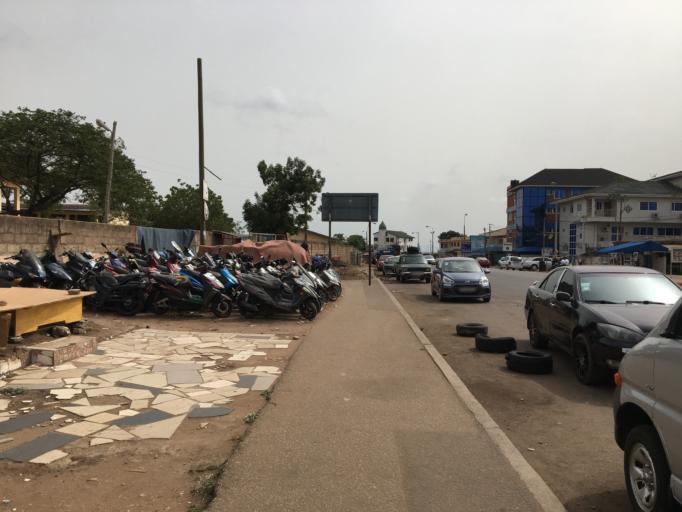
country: GH
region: Greater Accra
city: Accra
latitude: 5.5980
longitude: -0.1939
